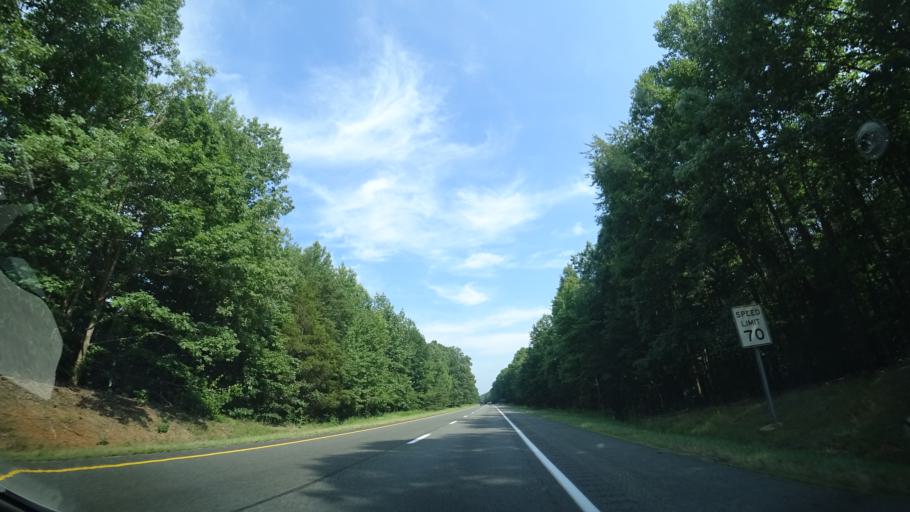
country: US
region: Virginia
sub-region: Louisa County
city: Louisa
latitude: 37.8773
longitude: -78.0228
